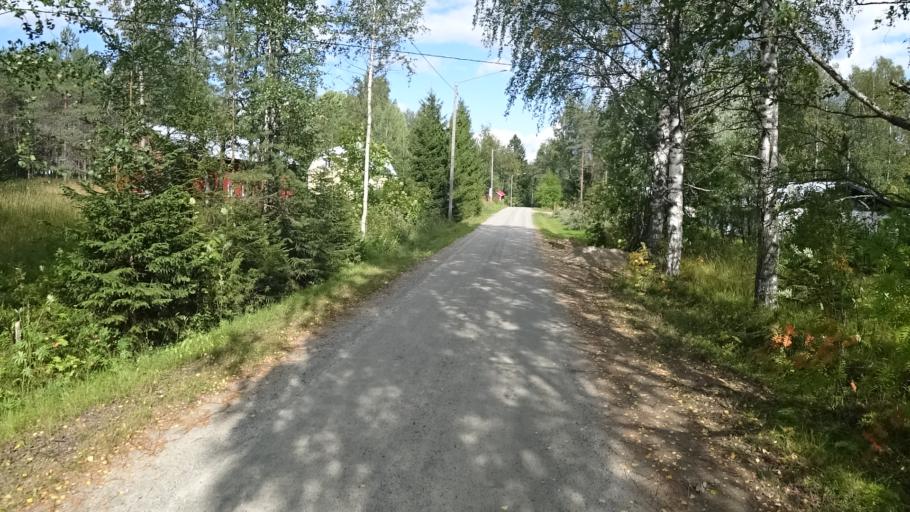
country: FI
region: North Karelia
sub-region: Joensuu
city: Ilomantsi
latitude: 62.6351
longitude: 31.2784
